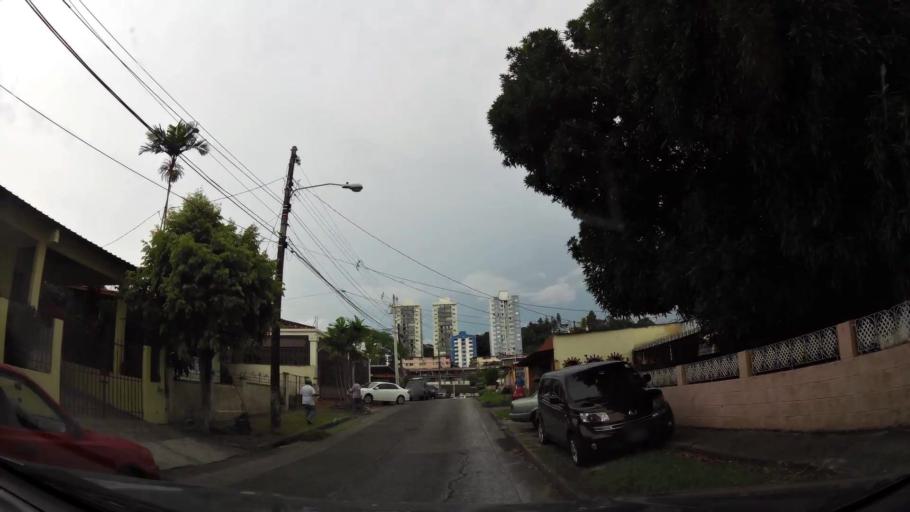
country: PA
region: Panama
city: Panama
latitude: 9.0191
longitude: -79.5283
